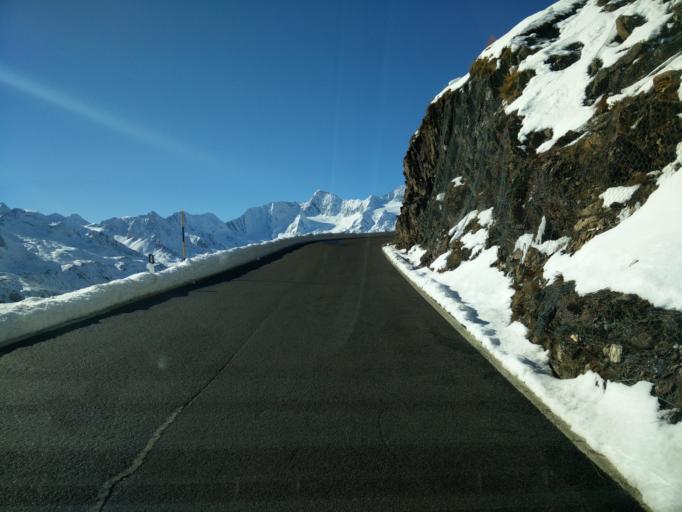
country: IT
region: Trentino-Alto Adige
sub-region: Bolzano
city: Moso in Passiria
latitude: 46.8917
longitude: 11.1190
